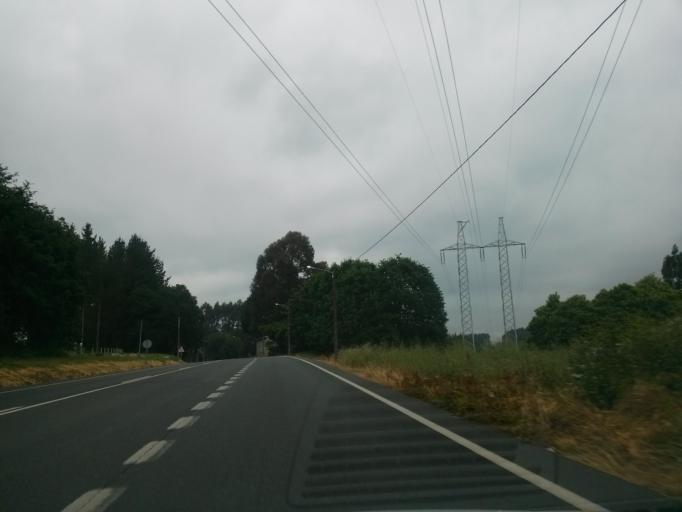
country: ES
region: Galicia
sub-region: Provincia de Lugo
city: Begonte
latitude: 43.1460
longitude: -7.6804
